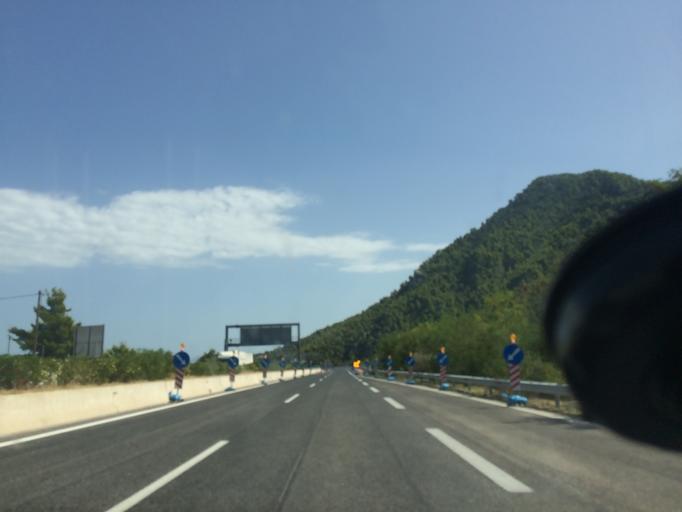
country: GR
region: Central Greece
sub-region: Nomos Fthiotidos
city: Ayios Konstandinos
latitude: 38.7525
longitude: 22.9042
